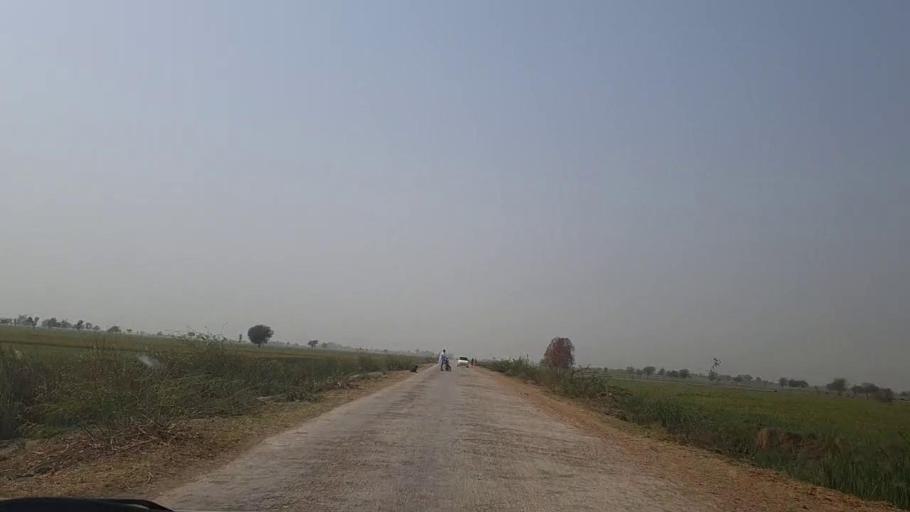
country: PK
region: Sindh
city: Pithoro
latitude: 25.5451
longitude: 69.2472
